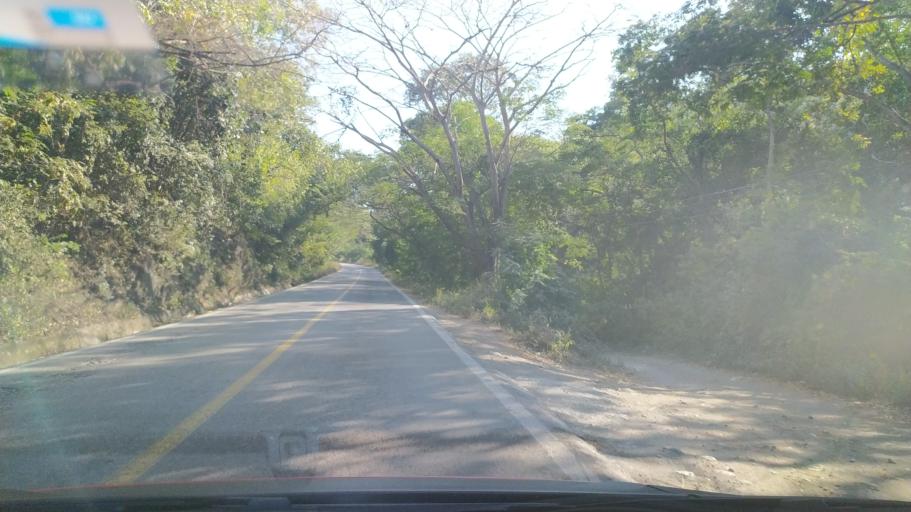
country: MX
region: Michoacan
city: Coahuayana Viejo
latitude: 18.6207
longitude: -103.6784
